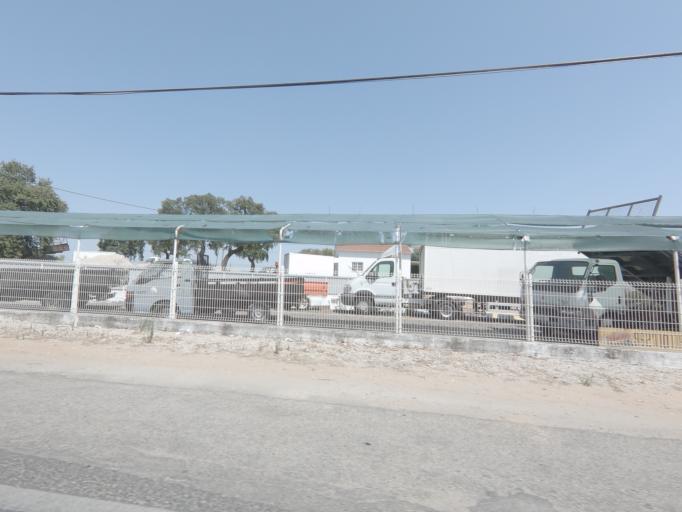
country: PT
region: Setubal
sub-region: Palmela
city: Palmela
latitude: 38.5655
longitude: -8.8875
